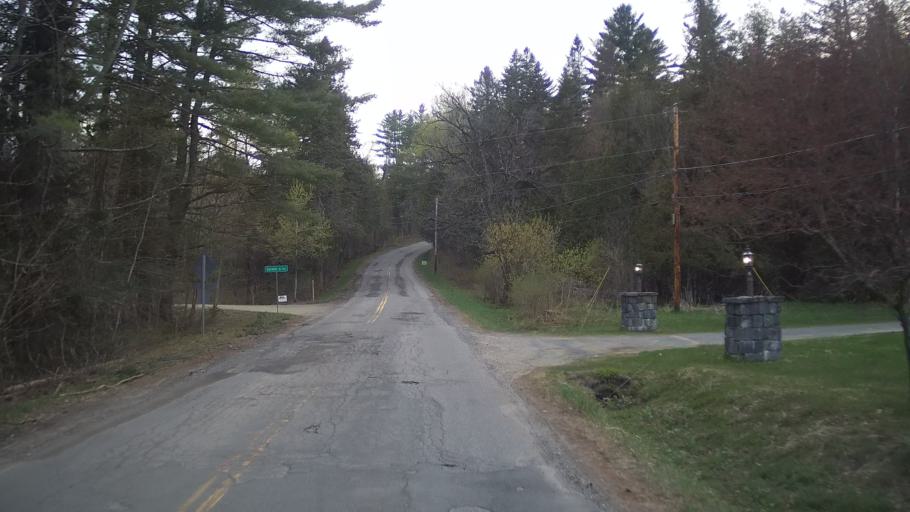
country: US
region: Vermont
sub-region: Caledonia County
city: Lyndonville
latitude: 44.5893
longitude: -71.9491
